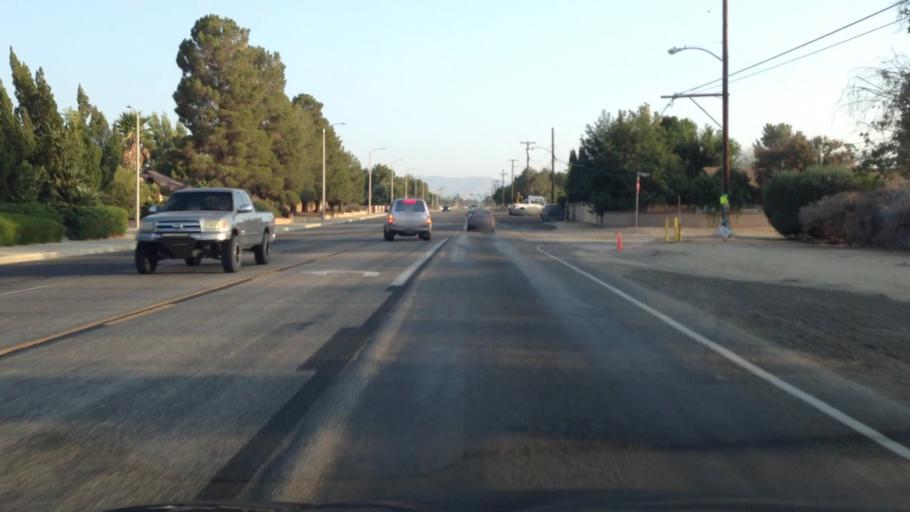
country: US
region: California
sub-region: Los Angeles County
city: Quartz Hill
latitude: 34.6571
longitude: -118.1834
